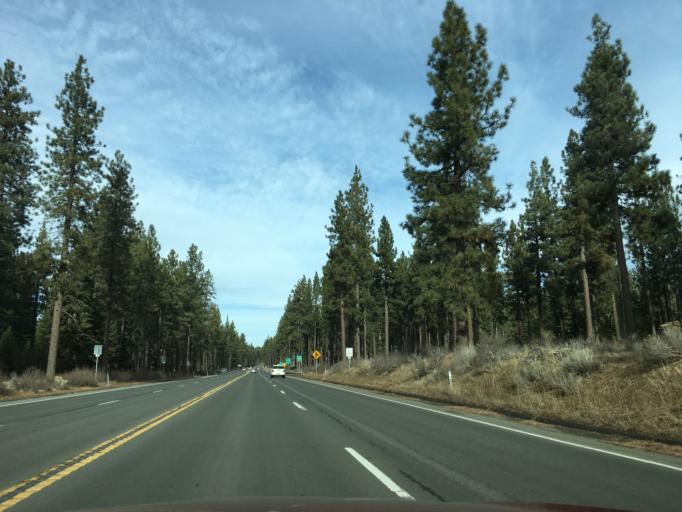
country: US
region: Nevada
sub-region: Douglas County
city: Kingsbury
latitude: 39.0084
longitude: -119.9472
